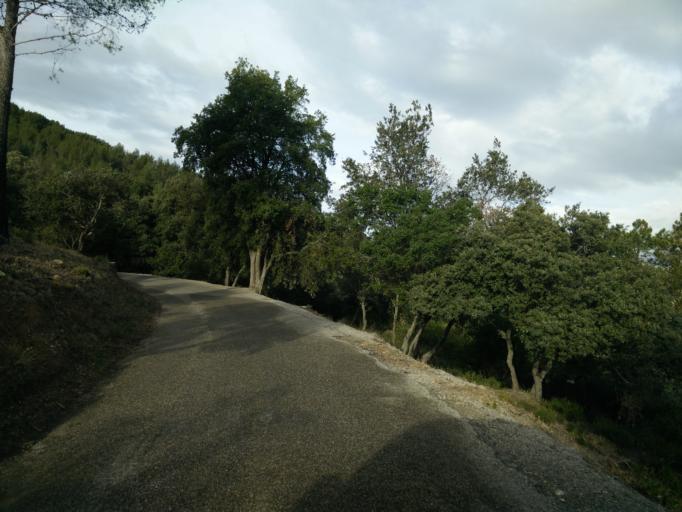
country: FR
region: Provence-Alpes-Cote d'Azur
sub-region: Departement du Var
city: Six-Fours-les-Plages
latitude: 43.0574
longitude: 5.8362
